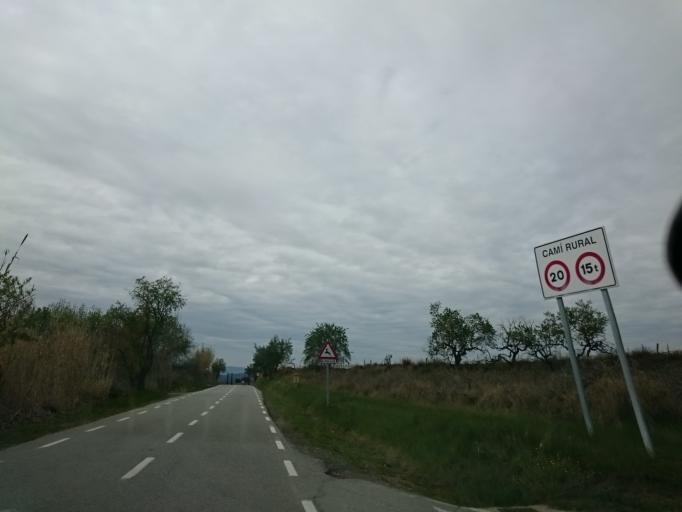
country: ES
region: Catalonia
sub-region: Provincia de Barcelona
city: Sant Llorenc d'Hortons
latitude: 41.4436
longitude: 1.8095
